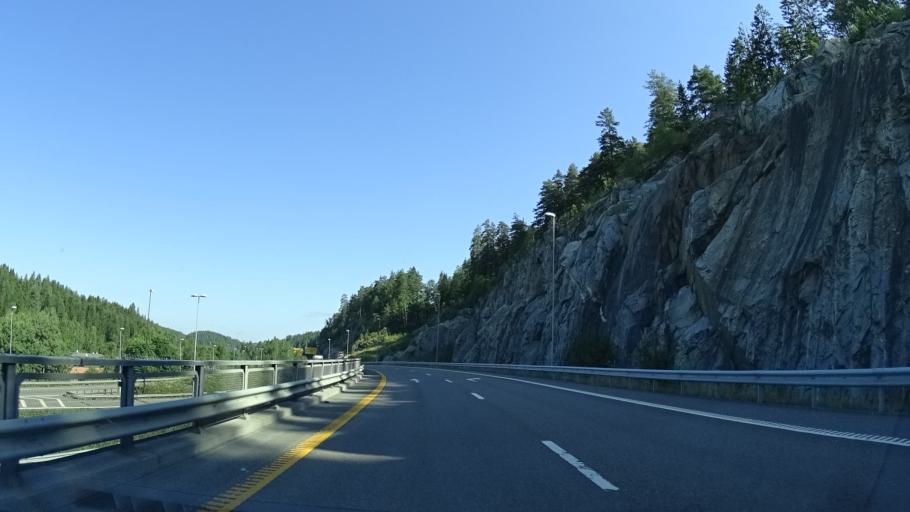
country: NO
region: Akershus
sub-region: Ski
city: Ski
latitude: 59.7511
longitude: 10.7845
